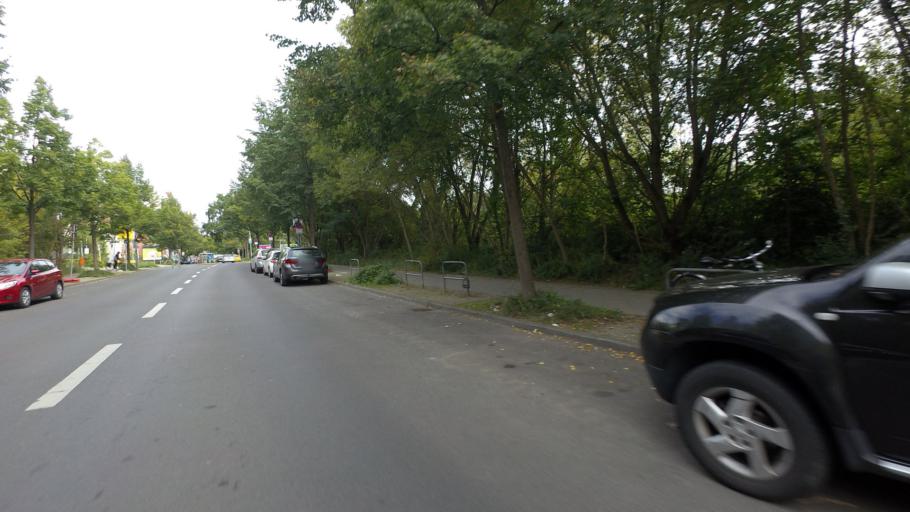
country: DE
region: Berlin
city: Wilhelmsruh
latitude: 52.5725
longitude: 13.3802
